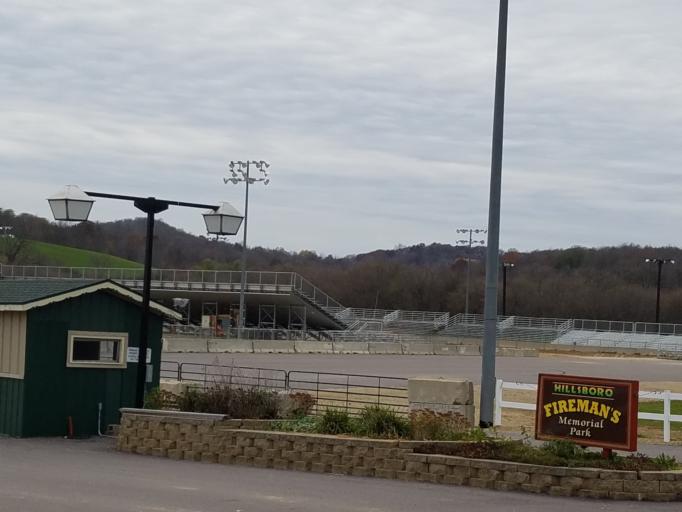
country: US
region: Wisconsin
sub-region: Vernon County
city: Hillsboro
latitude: 43.6528
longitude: -90.3538
